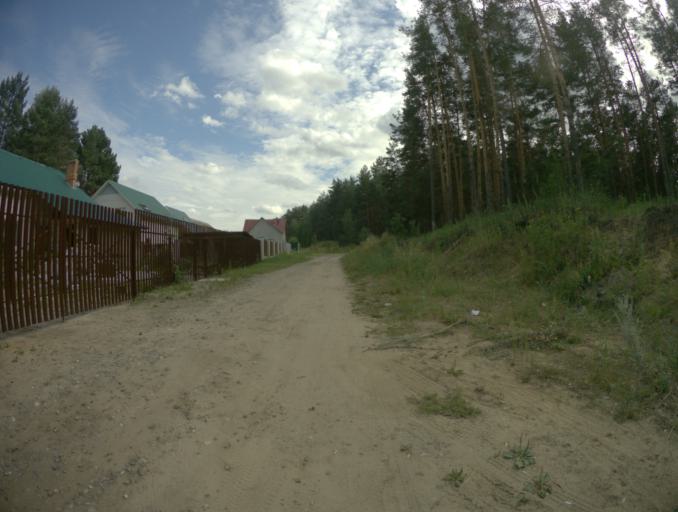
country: RU
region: Vladimir
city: Raduzhnyy
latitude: 56.0321
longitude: 40.3807
